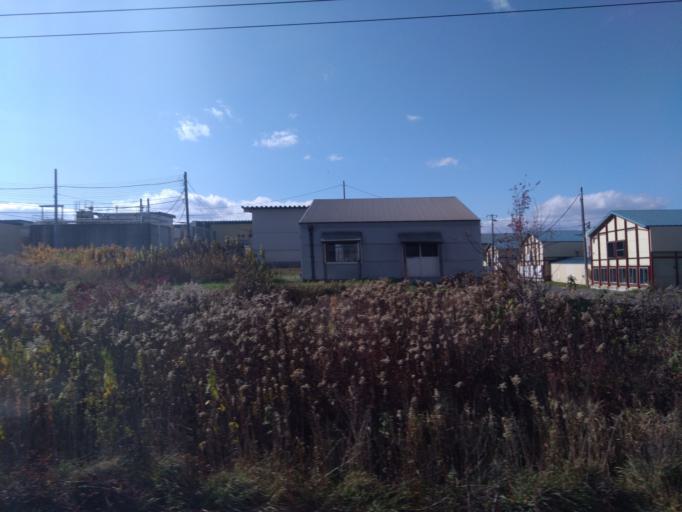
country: JP
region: Hokkaido
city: Kitahiroshima
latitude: 42.9562
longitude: 141.5697
